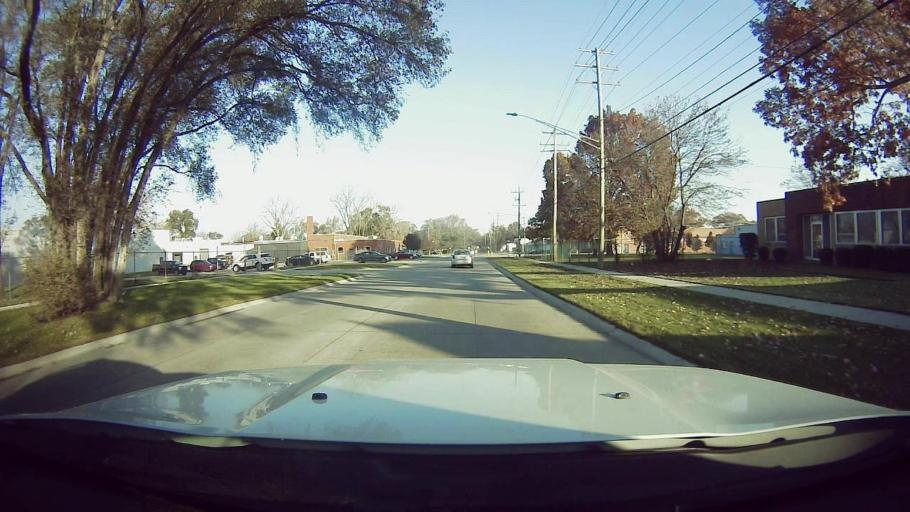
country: US
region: Michigan
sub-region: Oakland County
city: Oak Park
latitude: 42.4548
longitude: -83.1619
